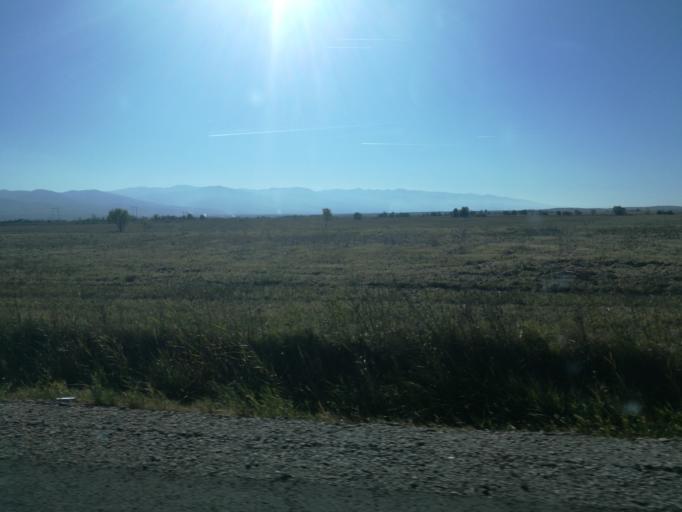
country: RO
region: Brasov
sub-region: Comuna Sinca Veche
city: Sinca Veche
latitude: 45.8030
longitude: 25.1761
